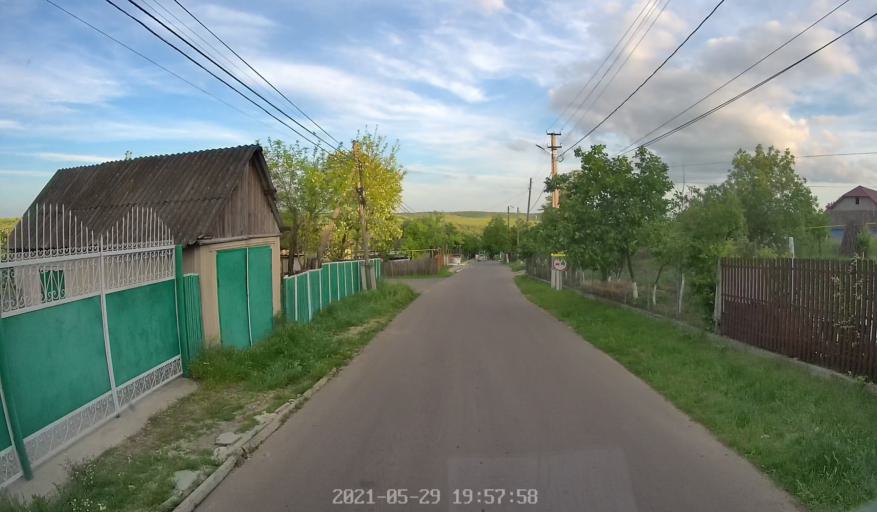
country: MD
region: Chisinau
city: Singera
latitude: 46.8315
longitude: 28.9725
